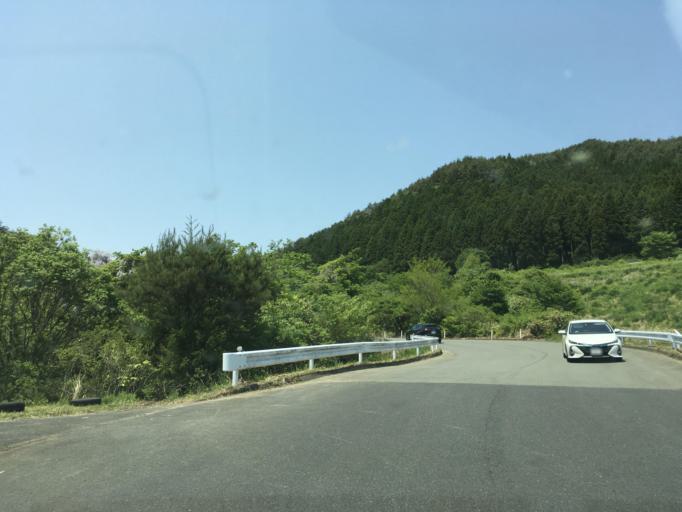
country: JP
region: Iwate
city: Ofunato
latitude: 38.8517
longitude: 141.4997
